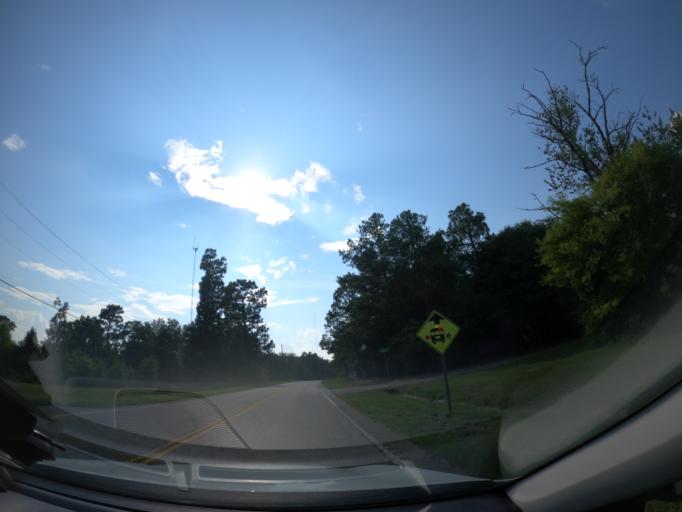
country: US
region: South Carolina
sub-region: Aiken County
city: Jackson
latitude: 33.4085
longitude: -81.8246
